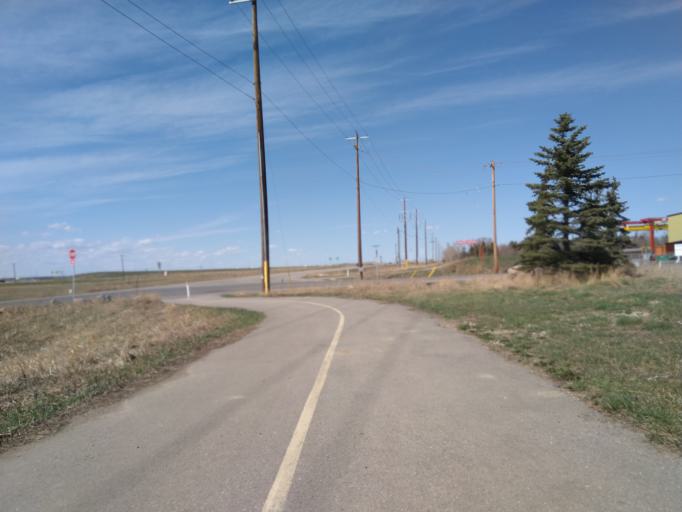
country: CA
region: Alberta
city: Chestermere
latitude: 50.9699
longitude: -113.9115
